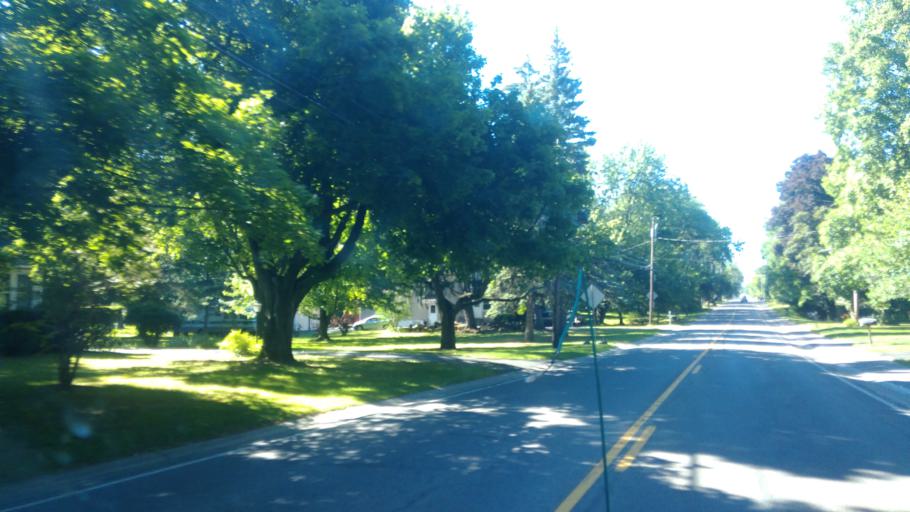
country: US
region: New York
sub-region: Monroe County
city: Webster
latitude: 43.2303
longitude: -77.4614
